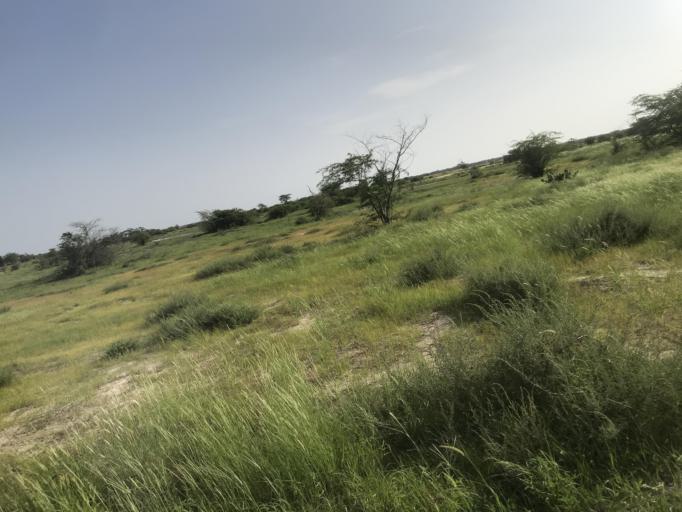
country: SN
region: Saint-Louis
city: Saint-Louis
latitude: 15.9305
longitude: -16.4598
